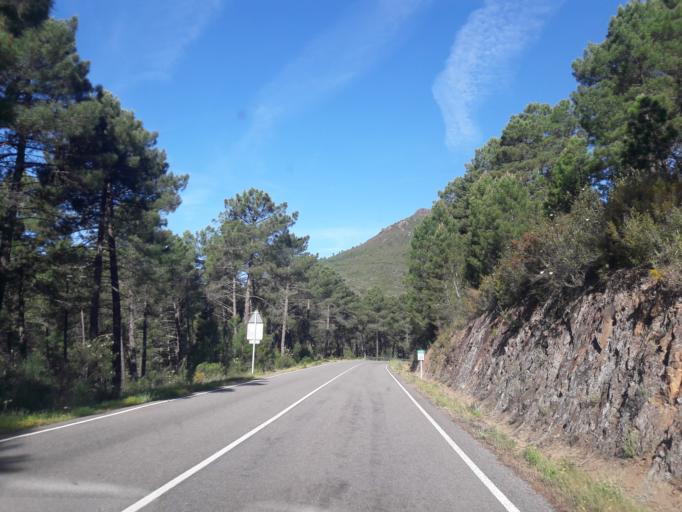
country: ES
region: Castille and Leon
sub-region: Provincia de Salamanca
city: Sotoserrano
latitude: 40.4117
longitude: -6.0441
